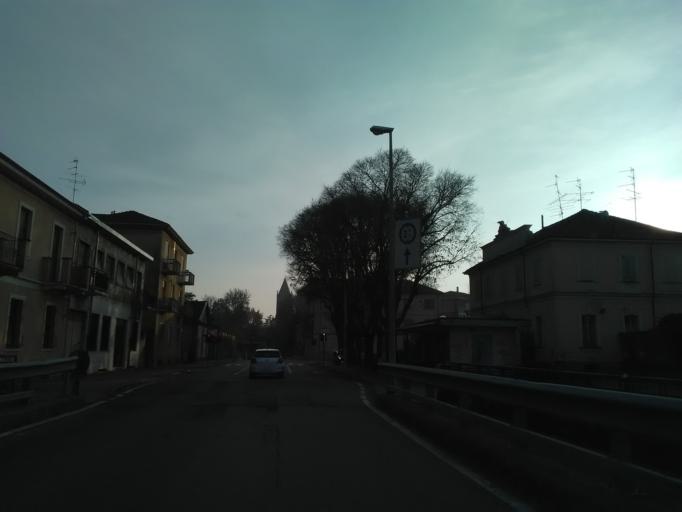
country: IT
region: Piedmont
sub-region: Provincia di Vercelli
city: Vercelli
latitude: 45.3328
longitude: 8.4205
